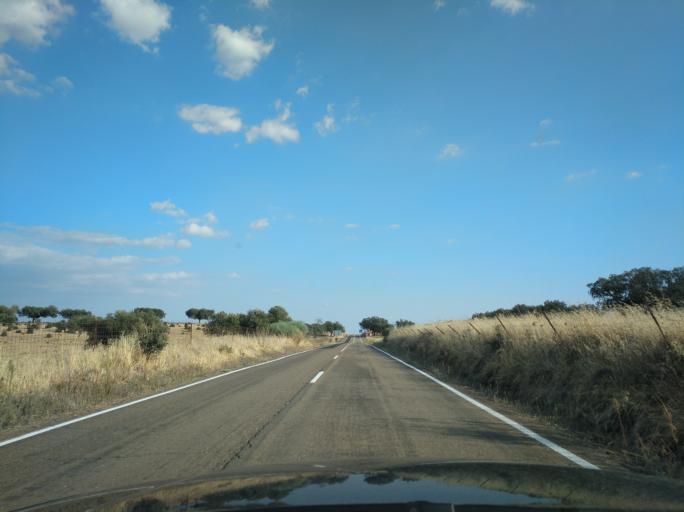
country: PT
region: Portalegre
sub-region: Campo Maior
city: Campo Maior
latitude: 39.1190
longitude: -7.0566
